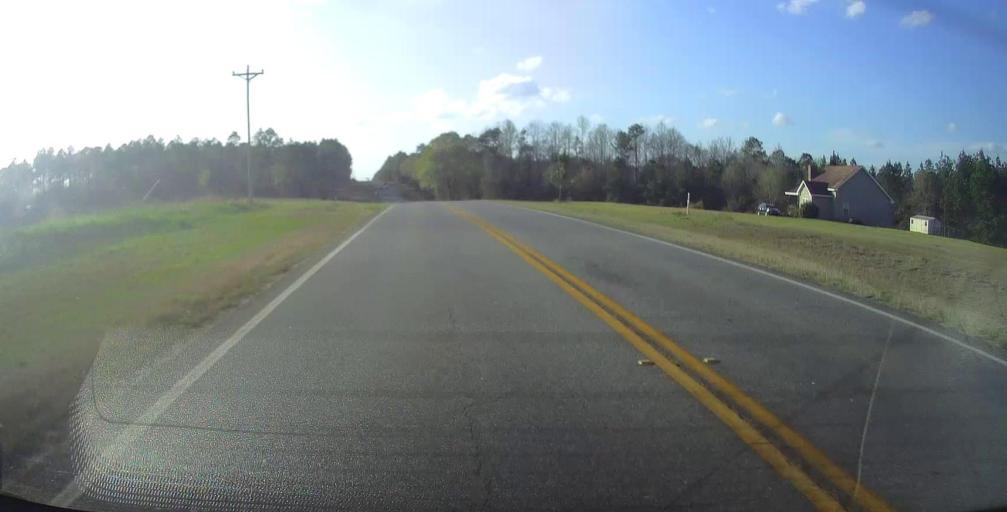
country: US
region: Georgia
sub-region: Toombs County
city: Lyons
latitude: 32.1349
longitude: -82.2270
